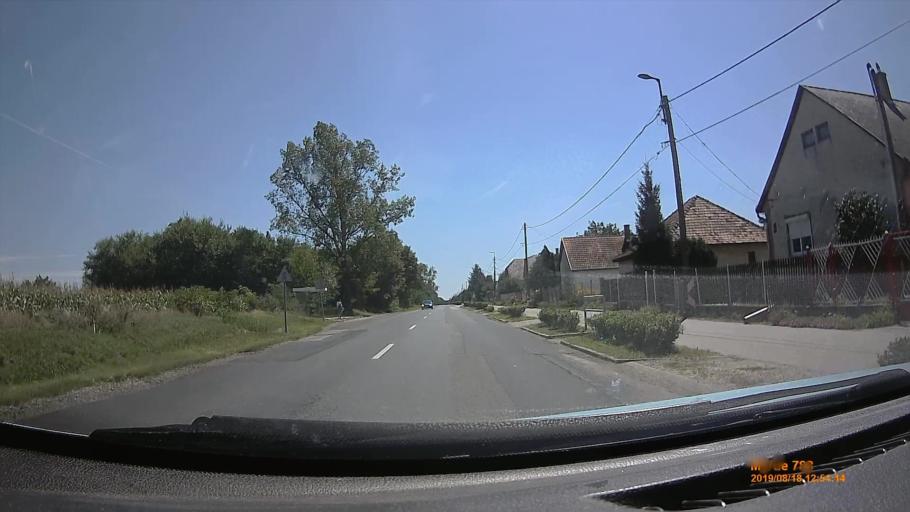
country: HU
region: Fejer
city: Aba
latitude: 47.0432
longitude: 18.5302
